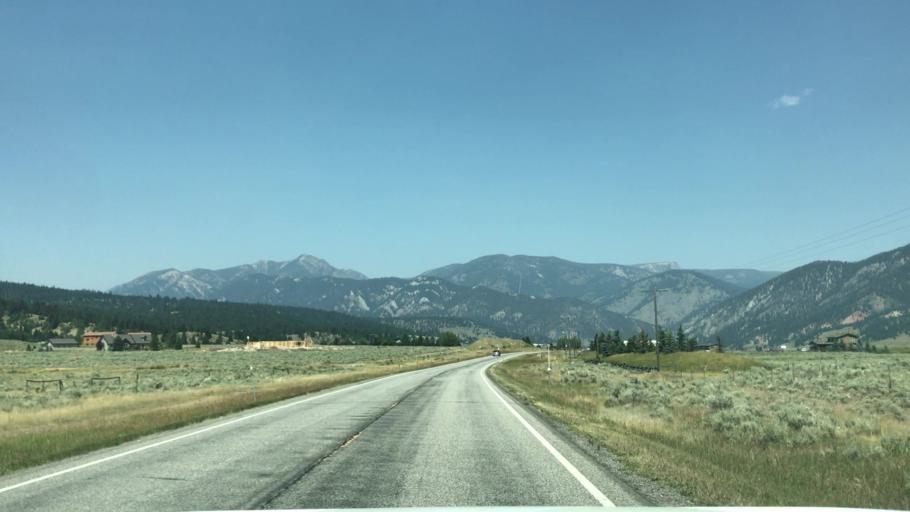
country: US
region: Montana
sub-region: Gallatin County
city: Big Sky
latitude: 45.2189
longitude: -111.2500
